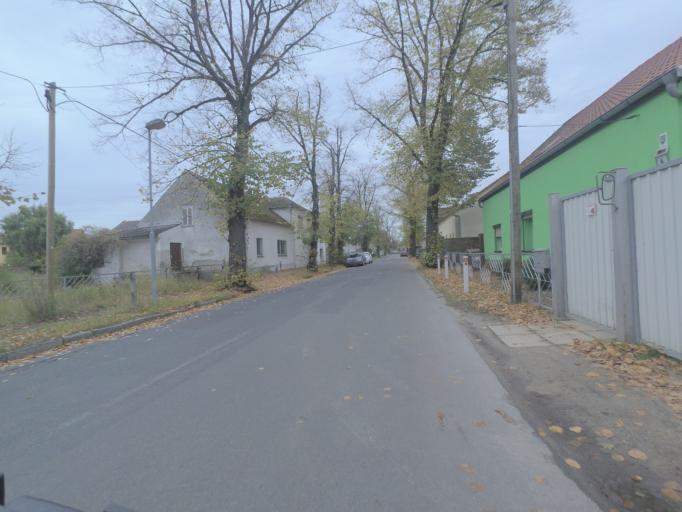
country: DE
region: Brandenburg
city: Rangsdorf
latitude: 52.2710
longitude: 13.3543
